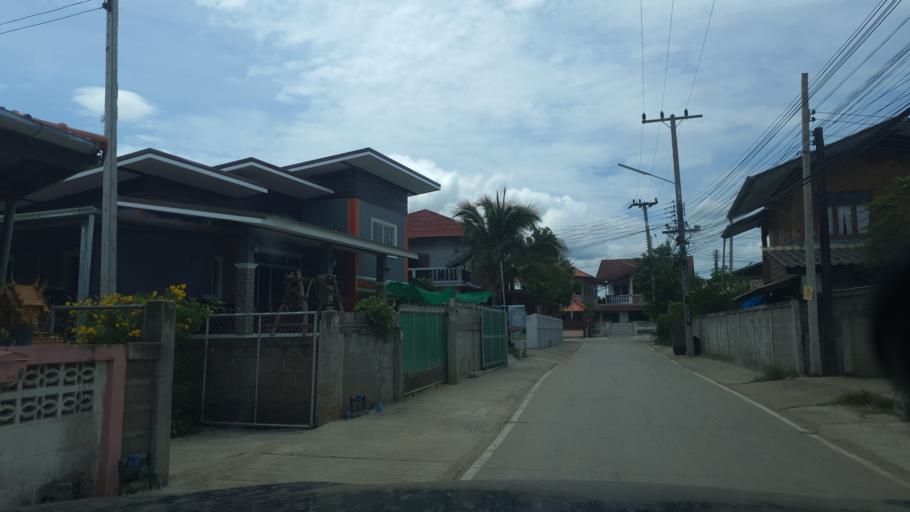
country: TH
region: Lampang
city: Sop Prap
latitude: 17.8817
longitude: 99.3830
